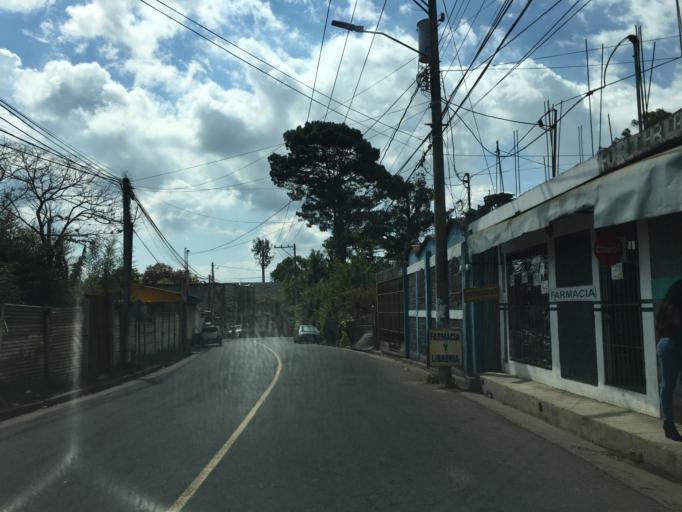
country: GT
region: Guatemala
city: San Jose Pinula
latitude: 14.5554
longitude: -90.4488
